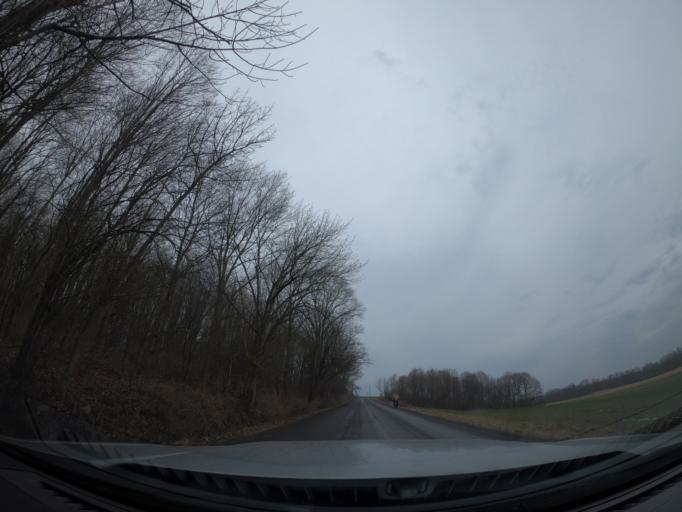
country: US
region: New York
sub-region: Cayuga County
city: Melrose Park
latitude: 42.8402
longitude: -76.5301
